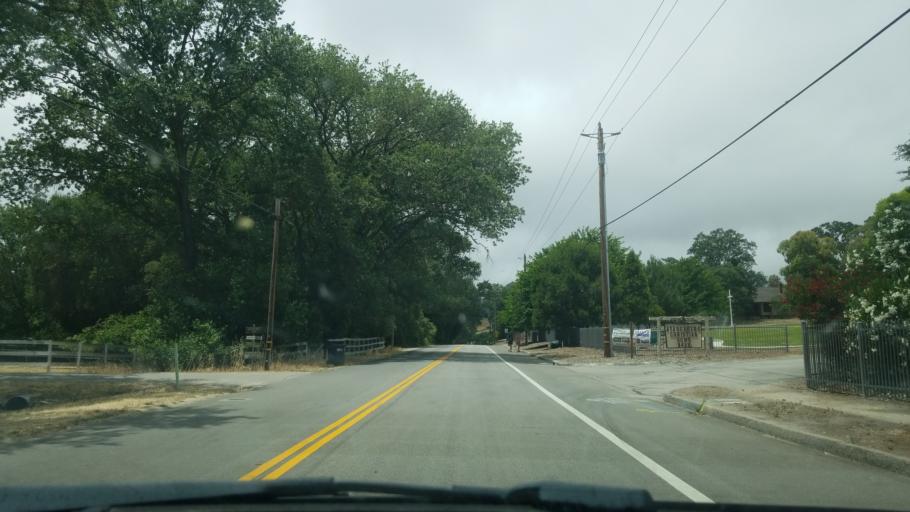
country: US
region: California
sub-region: San Luis Obispo County
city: Atascadero
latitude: 35.4633
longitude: -120.6593
